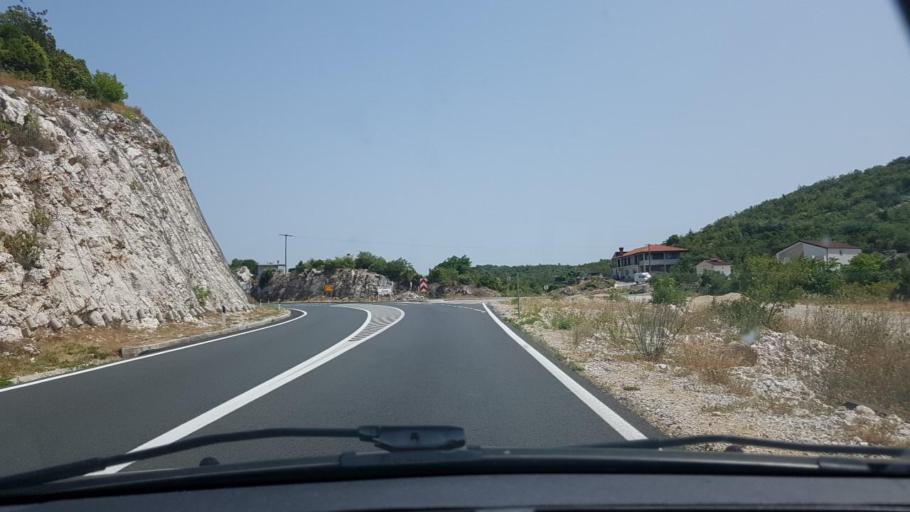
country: BA
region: Federation of Bosnia and Herzegovina
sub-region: Hercegovacko-Bosanski Kanton
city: Neum
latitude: 42.9257
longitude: 17.6335
